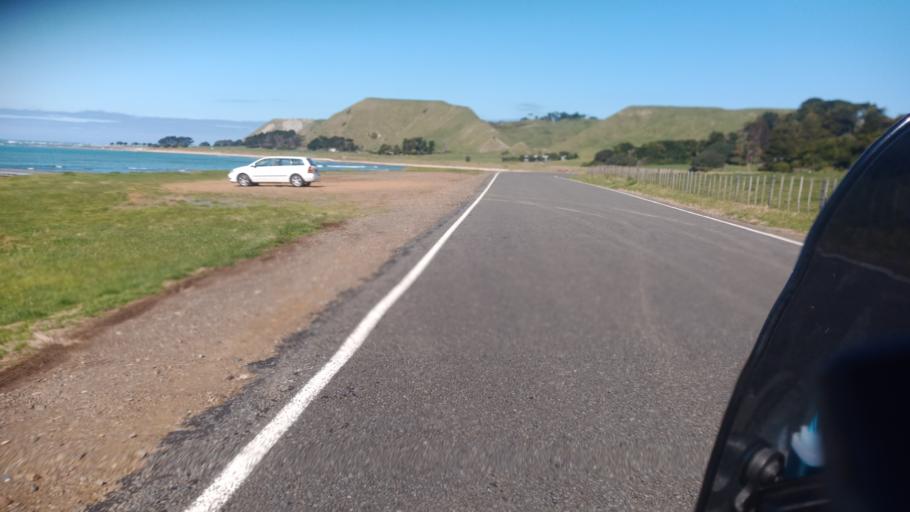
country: NZ
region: Gisborne
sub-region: Gisborne District
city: Gisborne
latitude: -39.0950
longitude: 177.9624
